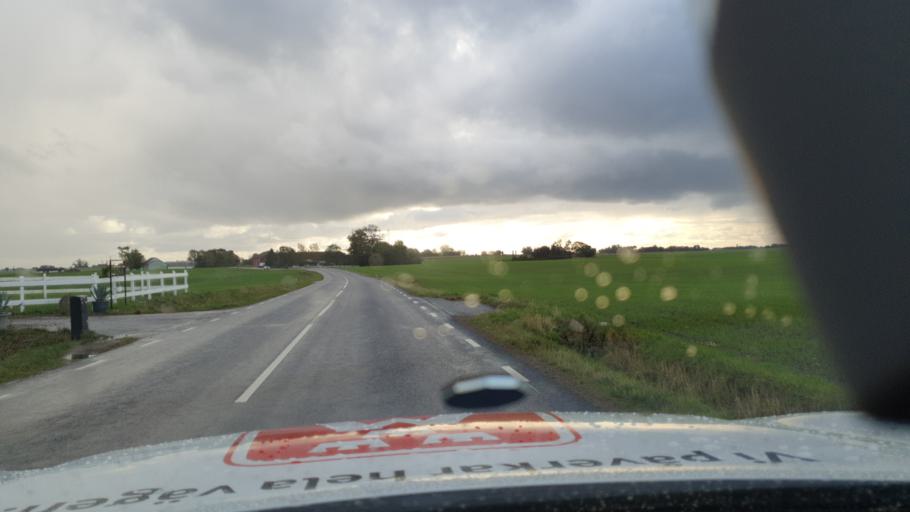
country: SE
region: Skane
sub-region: Trelleborgs Kommun
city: Anderslov
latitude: 55.4321
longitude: 13.3093
